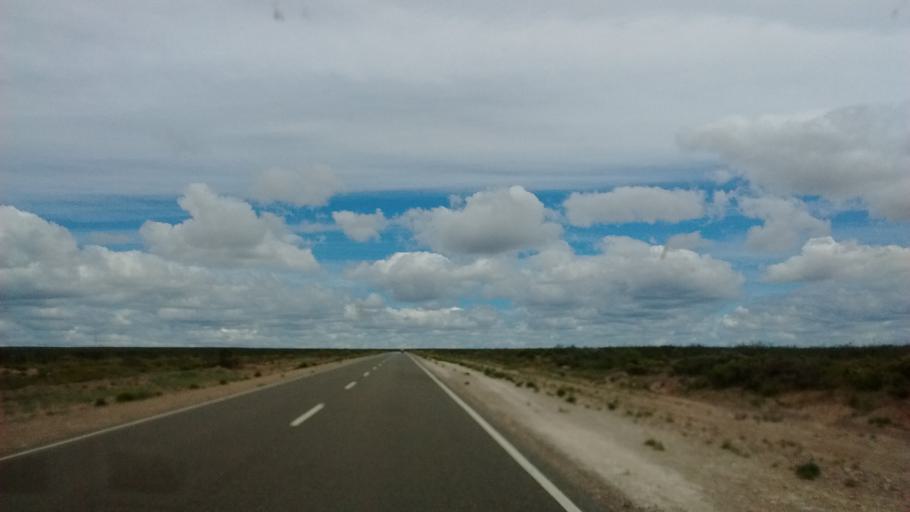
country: AR
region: Neuquen
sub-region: Departamento de Picun Leufu
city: Picun Leufu
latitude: -39.7452
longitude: -69.6113
